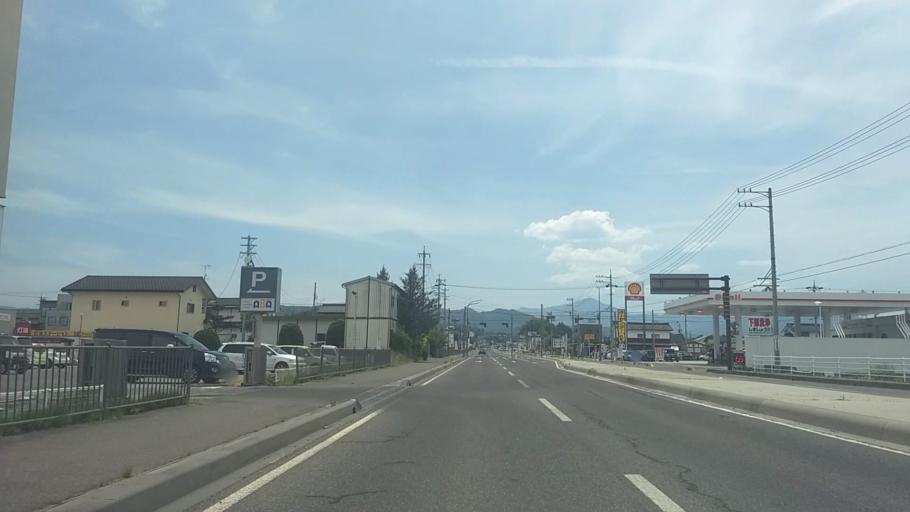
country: JP
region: Nagano
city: Saku
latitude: 36.1980
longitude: 138.4736
